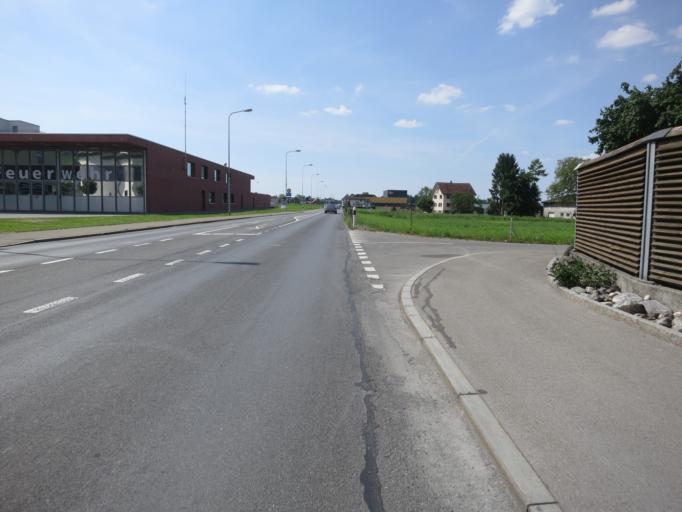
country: CH
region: Schwyz
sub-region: Bezirk March
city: Lachen
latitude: 47.1829
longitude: 8.8737
